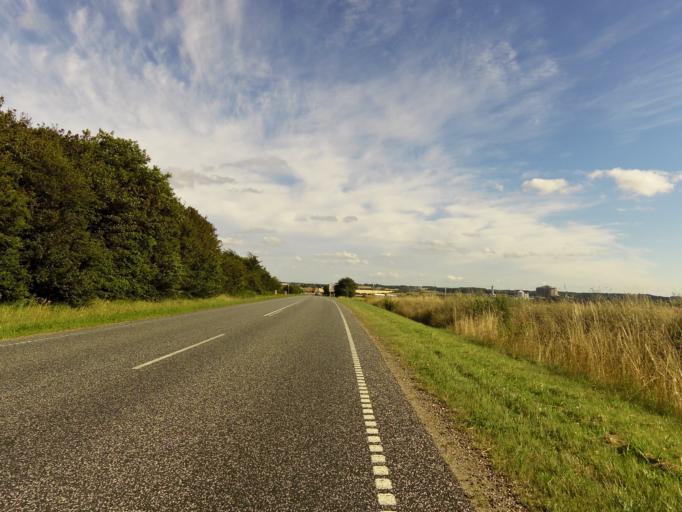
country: DK
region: South Denmark
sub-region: Tonder Kommune
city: Toftlund
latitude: 55.1833
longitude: 9.0599
